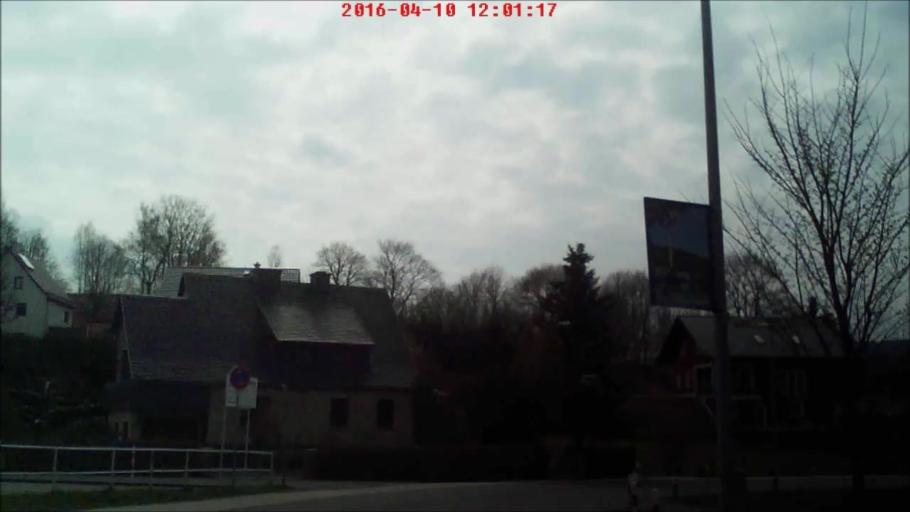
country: DE
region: Thuringia
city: Zella-Mehlis
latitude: 50.6675
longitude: 10.6654
